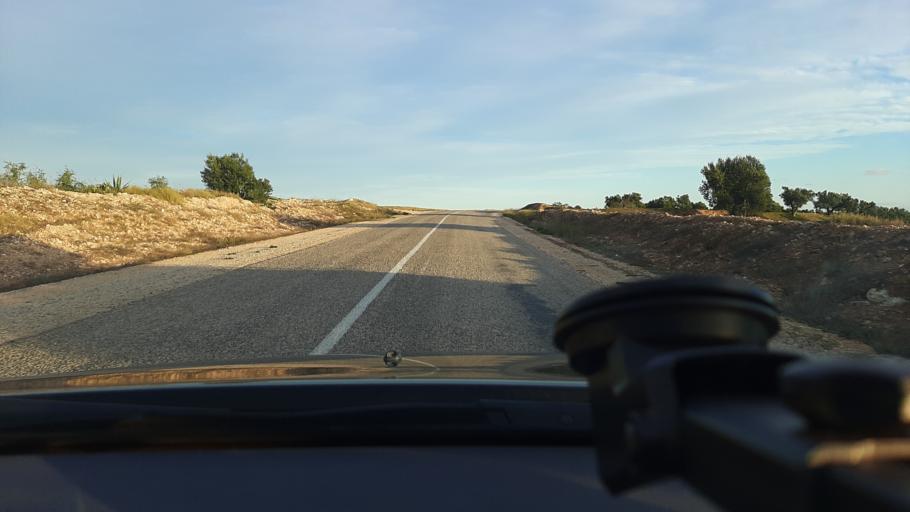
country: TN
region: Safaqis
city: Sfax
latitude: 34.9554
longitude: 10.5469
